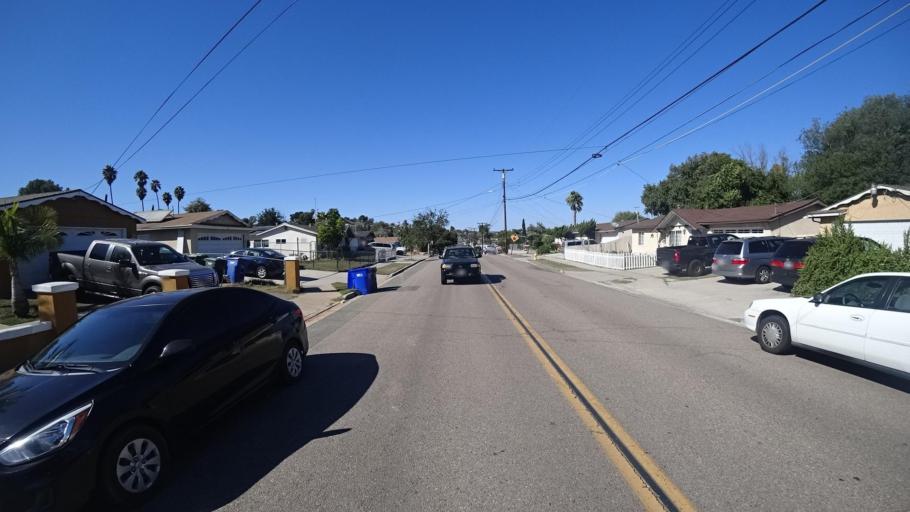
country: US
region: California
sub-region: San Diego County
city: La Presa
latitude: 32.7009
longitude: -117.0176
